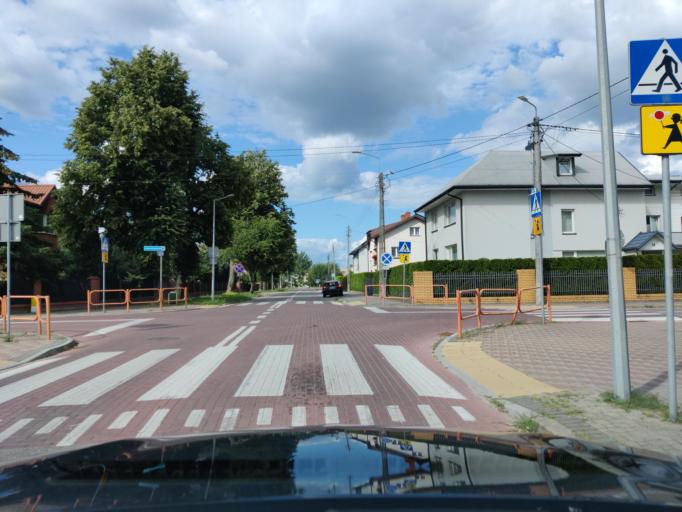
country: PL
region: Podlasie
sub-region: Powiat zambrowski
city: Zambrow
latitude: 52.9886
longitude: 22.2446
